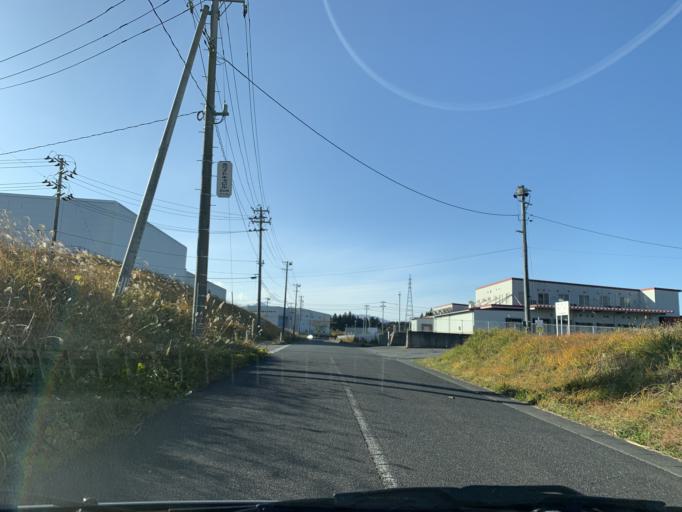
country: JP
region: Iwate
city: Kitakami
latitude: 39.2472
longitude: 141.0942
